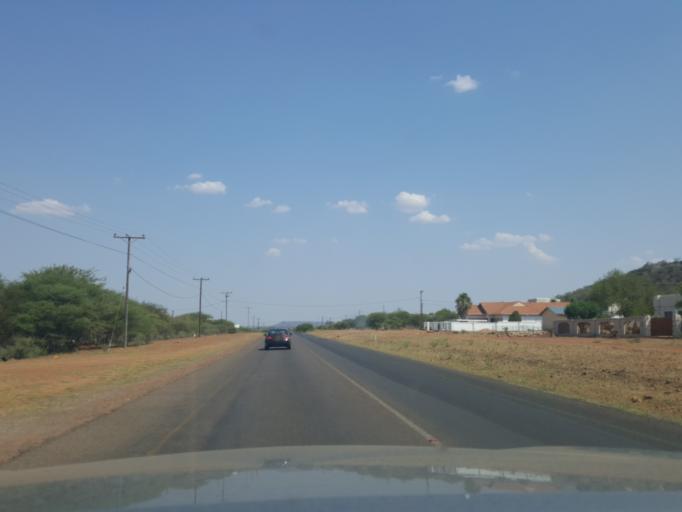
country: BW
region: South East
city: Ramotswa
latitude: -24.8349
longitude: 25.8166
